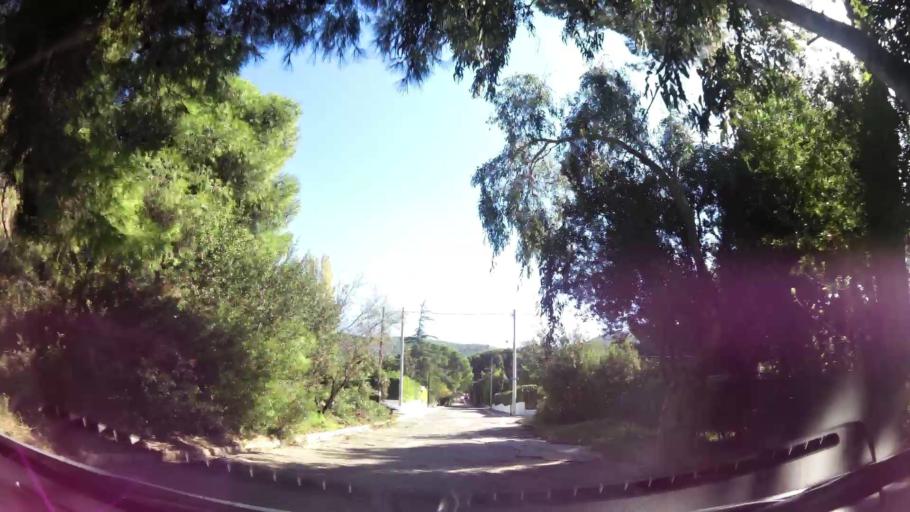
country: GR
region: Attica
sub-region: Nomarchia Athinas
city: Ekali
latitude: 38.1058
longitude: 23.8296
